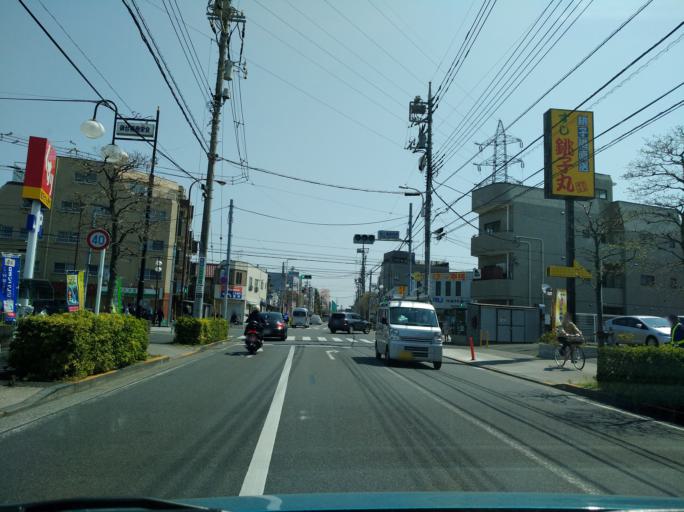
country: JP
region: Tokyo
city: Chofugaoka
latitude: 35.6415
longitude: 139.5753
